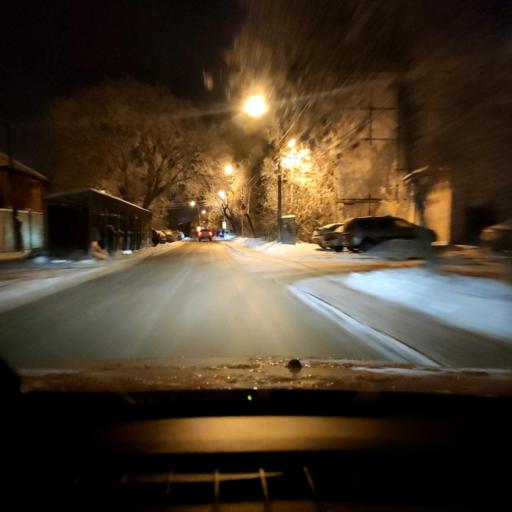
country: RU
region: Samara
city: Novosemeykino
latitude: 53.3456
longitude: 50.2281
